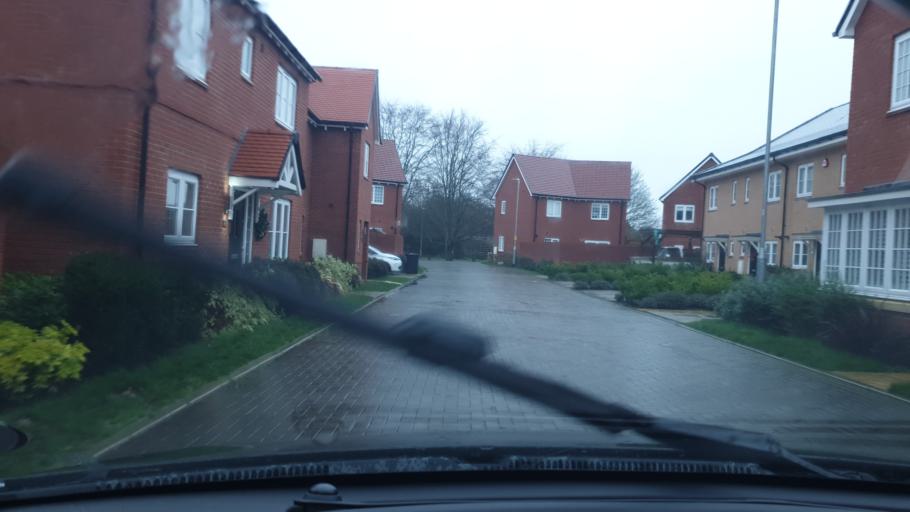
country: GB
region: England
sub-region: Essex
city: Great Horkesley
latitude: 51.9215
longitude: 0.8939
